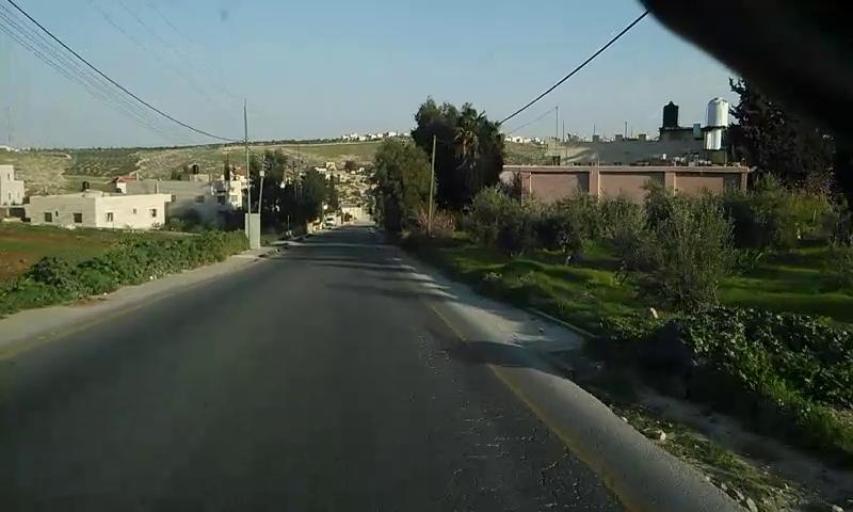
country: PS
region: West Bank
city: Jannatah
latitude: 31.6502
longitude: 35.2152
